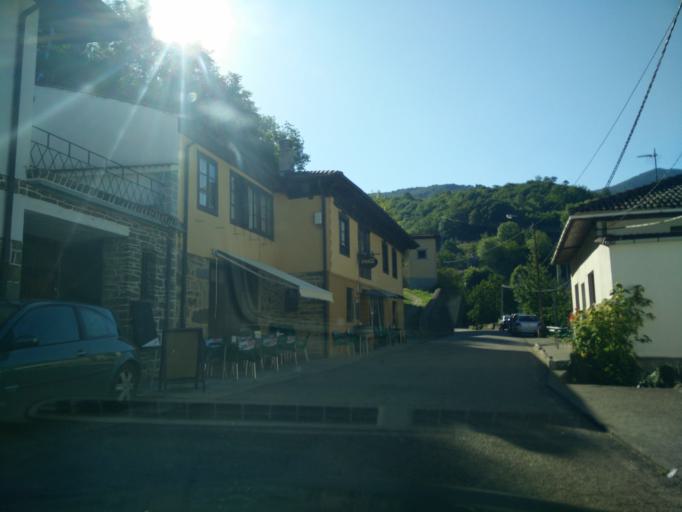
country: ES
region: Asturias
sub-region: Province of Asturias
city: Amieva
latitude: 43.1906
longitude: -5.1651
